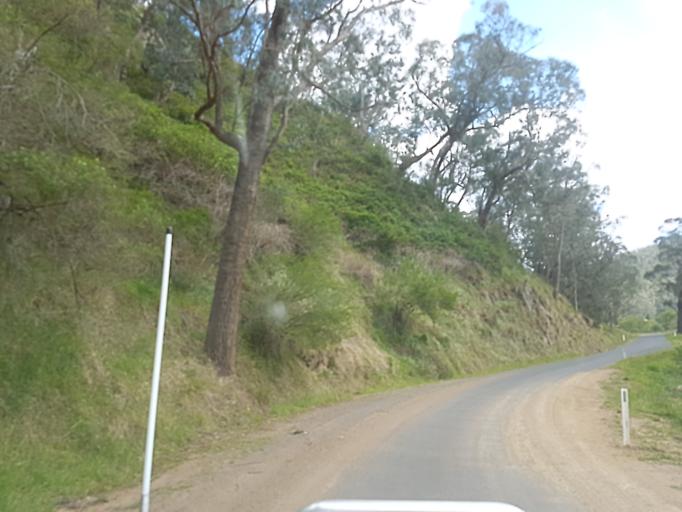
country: AU
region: Victoria
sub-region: East Gippsland
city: Bairnsdale
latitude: -37.4297
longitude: 147.2509
